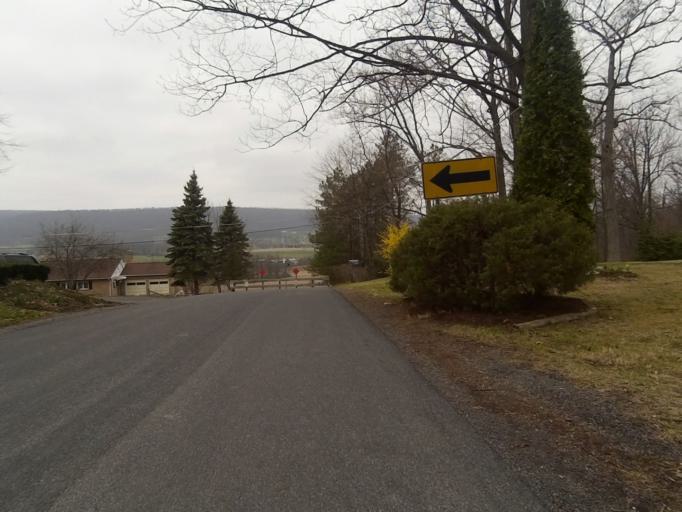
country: US
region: Pennsylvania
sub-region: Centre County
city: Boalsburg
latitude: 40.7871
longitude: -77.7731
